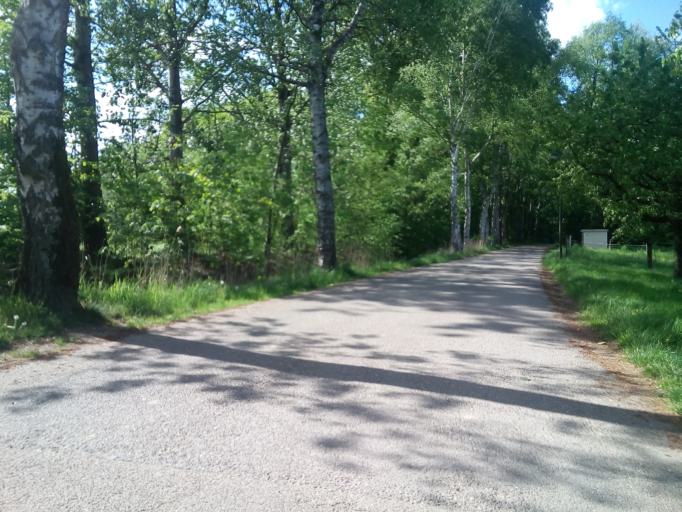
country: DE
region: Baden-Wuerttemberg
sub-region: Karlsruhe Region
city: Lichtenau
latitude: 48.7044
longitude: 7.9982
